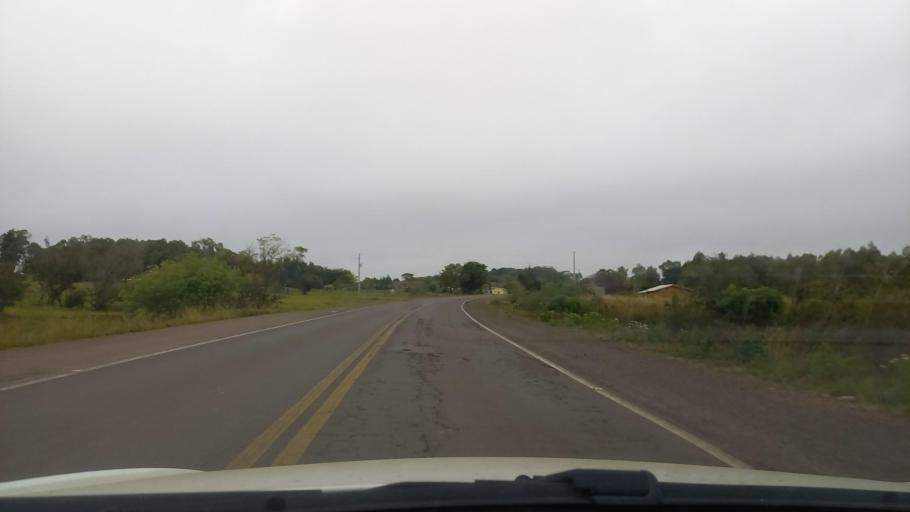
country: BR
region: Rio Grande do Sul
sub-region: Cacequi
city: Cacequi
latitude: -30.1211
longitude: -54.6390
